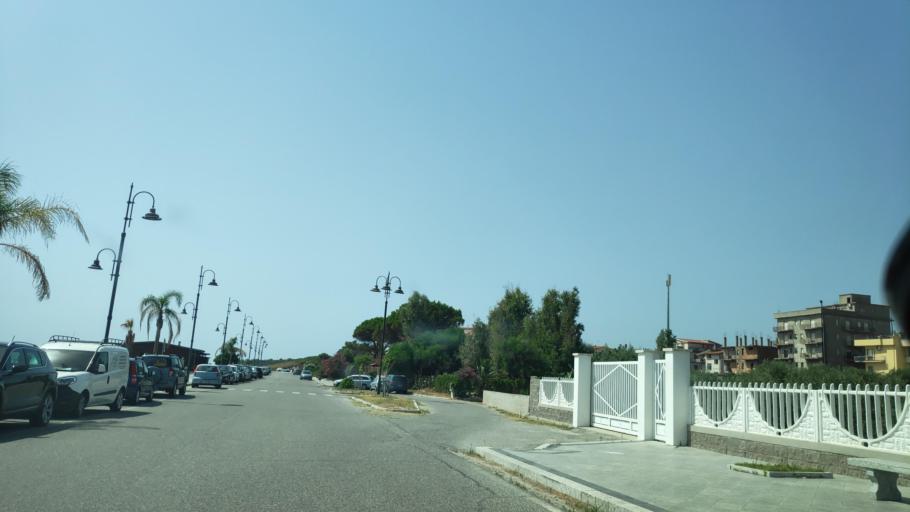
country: IT
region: Calabria
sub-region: Provincia di Catanzaro
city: Guardavalle Marina
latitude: 38.4805
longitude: 16.5801
